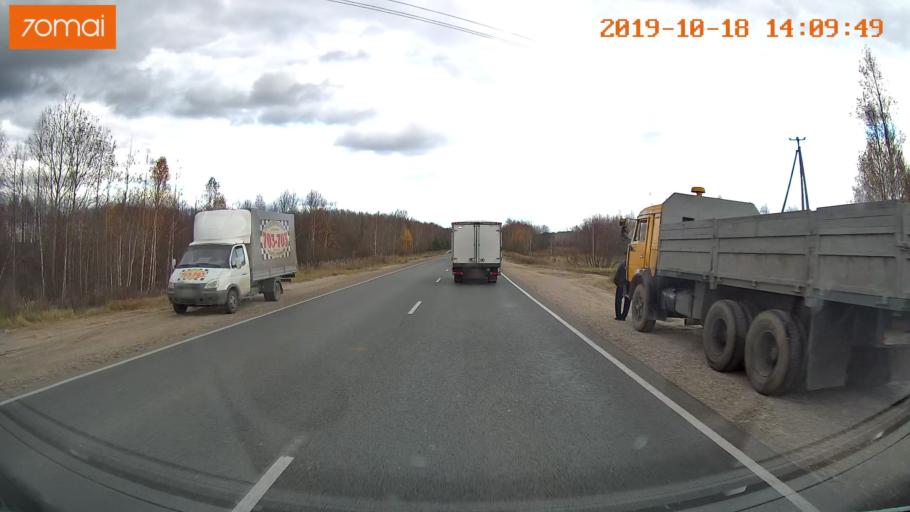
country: RU
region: Rjazan
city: Spas-Klepiki
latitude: 55.1439
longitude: 40.1931
